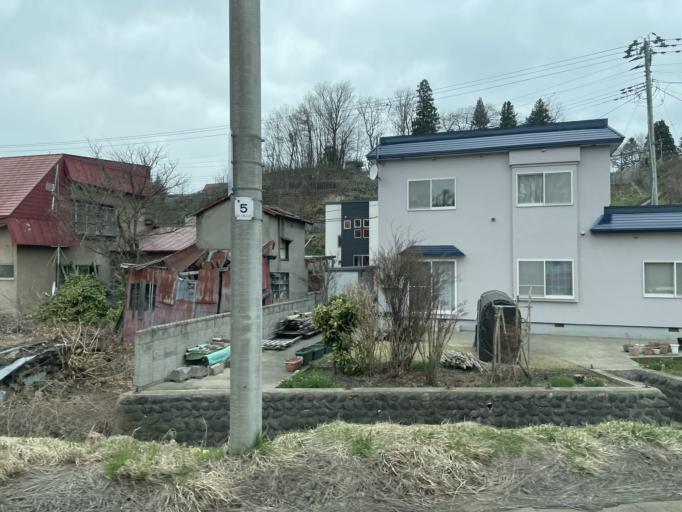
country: JP
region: Aomori
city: Aomori Shi
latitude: 40.8271
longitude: 140.6683
